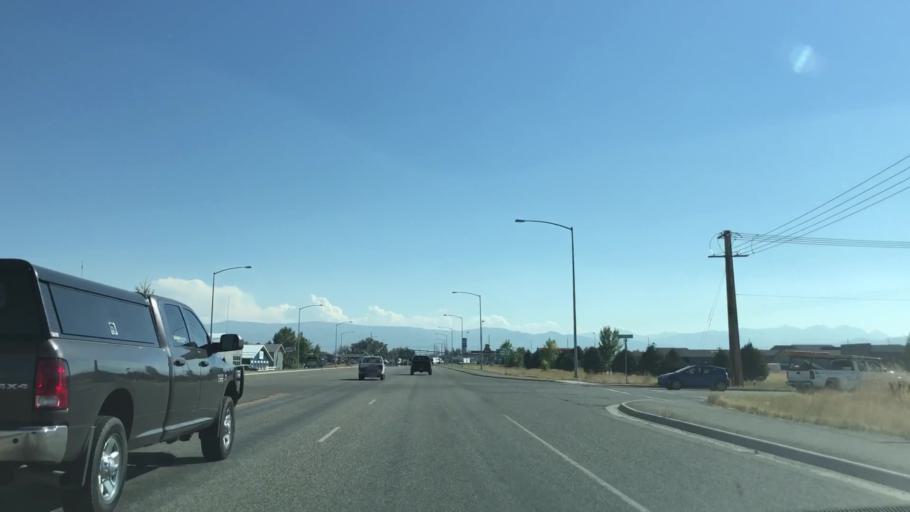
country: US
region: Montana
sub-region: Gallatin County
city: Four Corners
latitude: 45.6756
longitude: -111.1862
